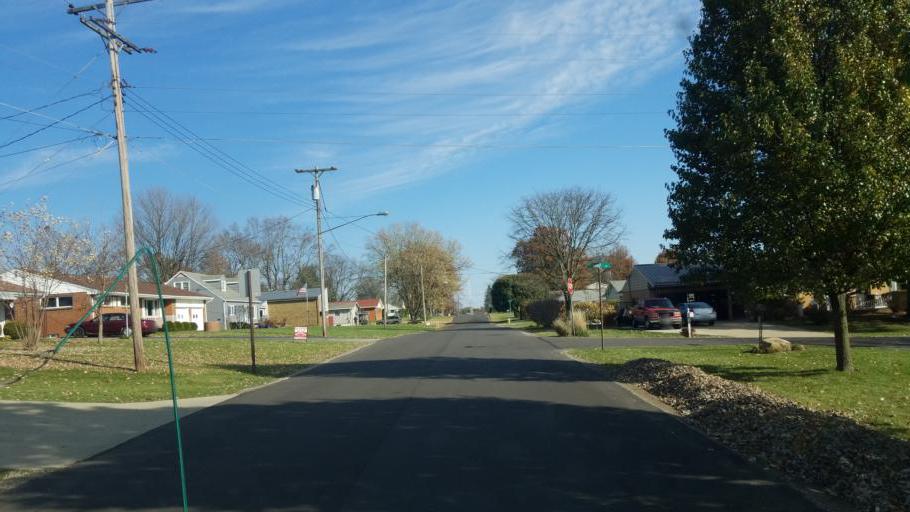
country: US
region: Ohio
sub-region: Richland County
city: Mansfield
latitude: 40.7227
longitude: -82.5363
